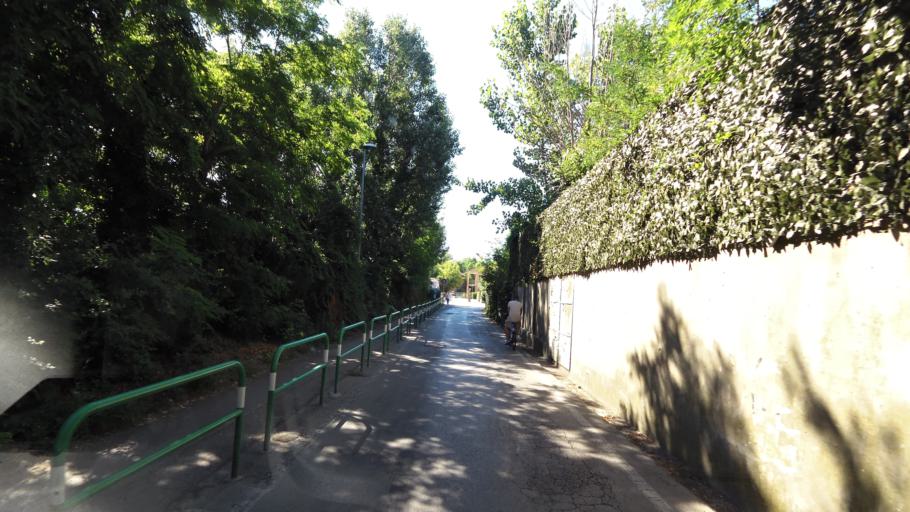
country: IT
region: Veneto
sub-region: Provincia di Venezia
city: Chioggia
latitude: 45.2103
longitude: 12.2916
